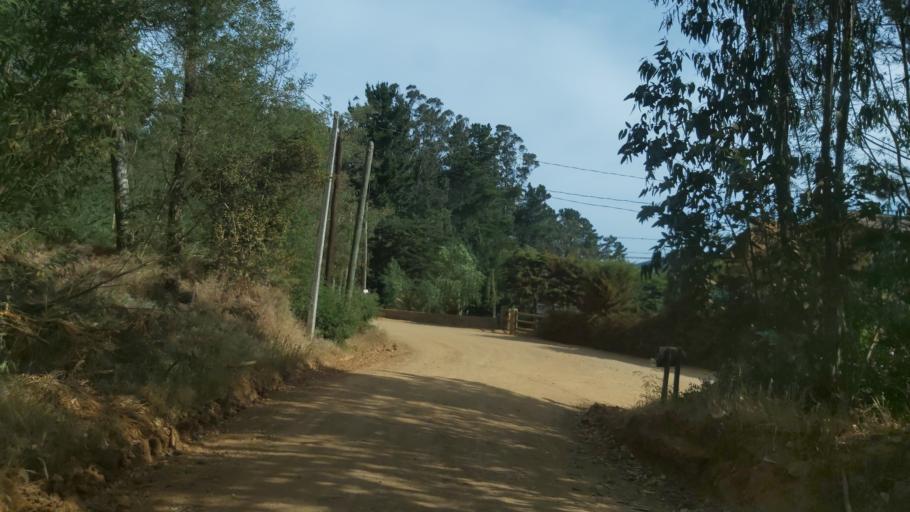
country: CL
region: Maule
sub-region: Provincia de Talca
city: Constitucion
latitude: -34.8438
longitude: -72.0403
